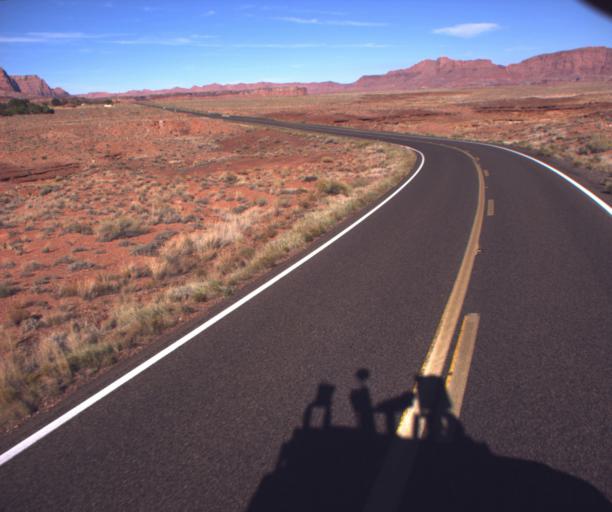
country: US
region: Arizona
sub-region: Coconino County
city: Page
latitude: 36.7804
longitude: -111.6903
